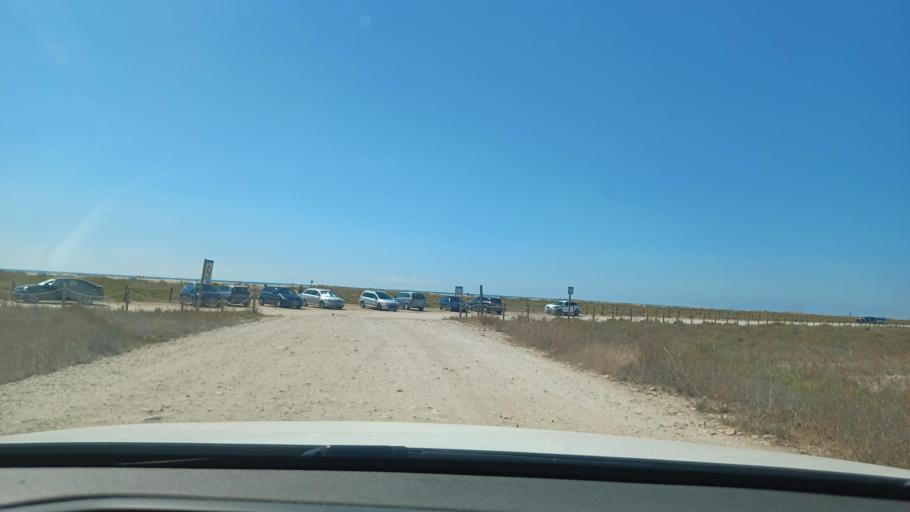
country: ES
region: Catalonia
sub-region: Provincia de Tarragona
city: Deltebre
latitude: 40.6468
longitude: 0.7635
